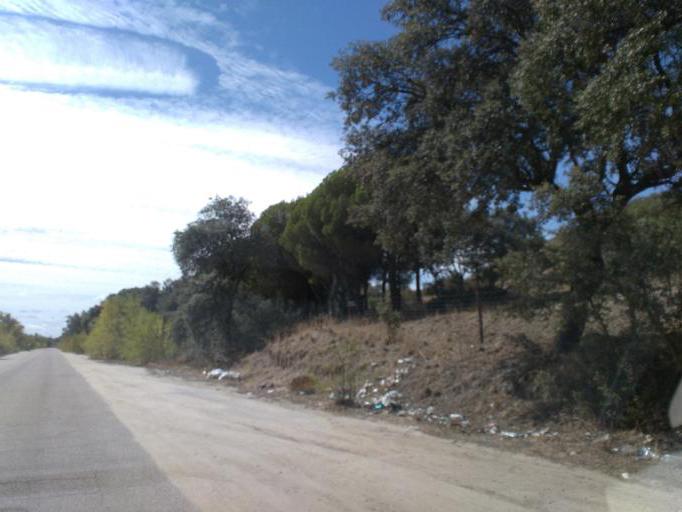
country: ES
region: Madrid
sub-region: Provincia de Madrid
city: Villanueva del Pardillo
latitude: 40.5264
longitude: -3.9422
